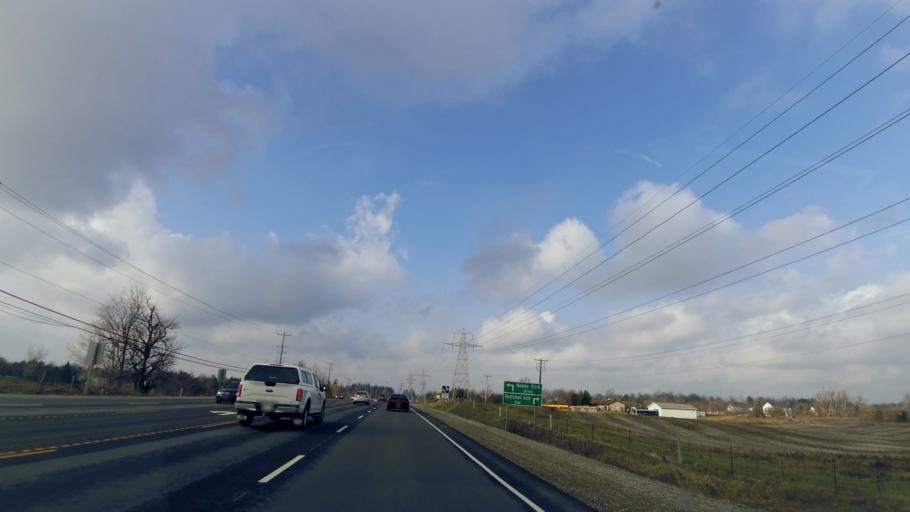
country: CA
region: Ontario
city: Ancaster
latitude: 43.3913
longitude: -80.0252
